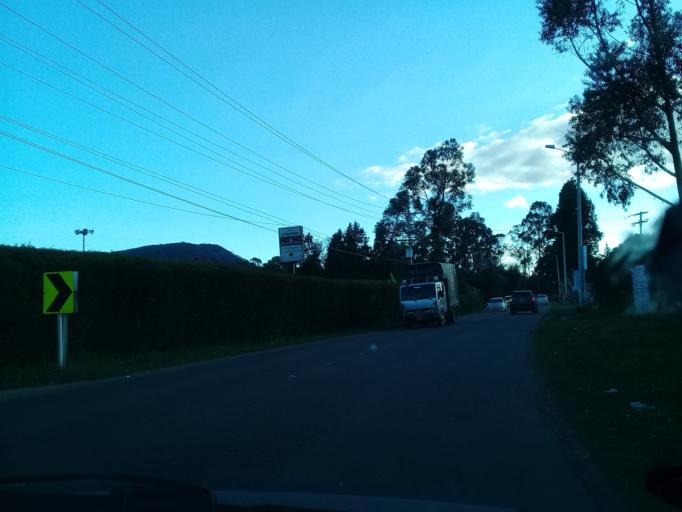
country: CO
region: Cundinamarca
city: Tenjo
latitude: 4.8548
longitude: -74.1334
